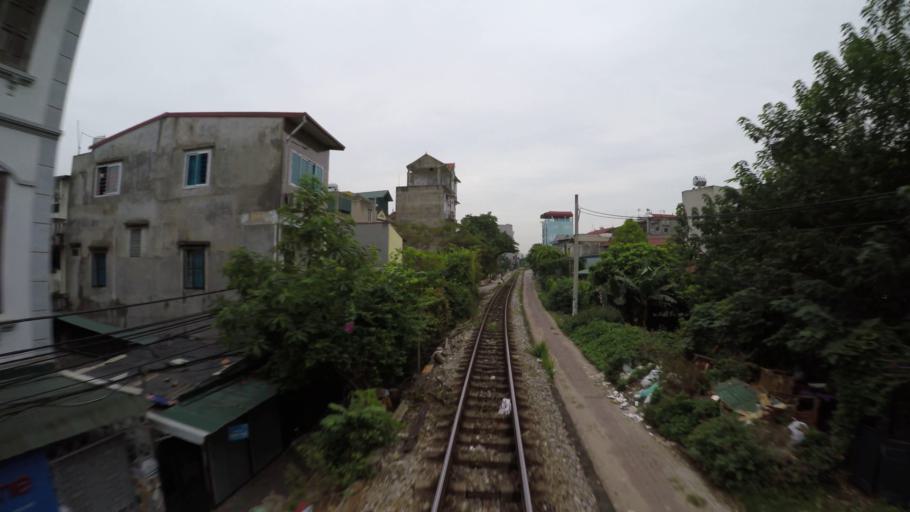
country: VN
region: Ha Noi
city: Trau Quy
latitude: 21.0214
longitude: 105.9367
